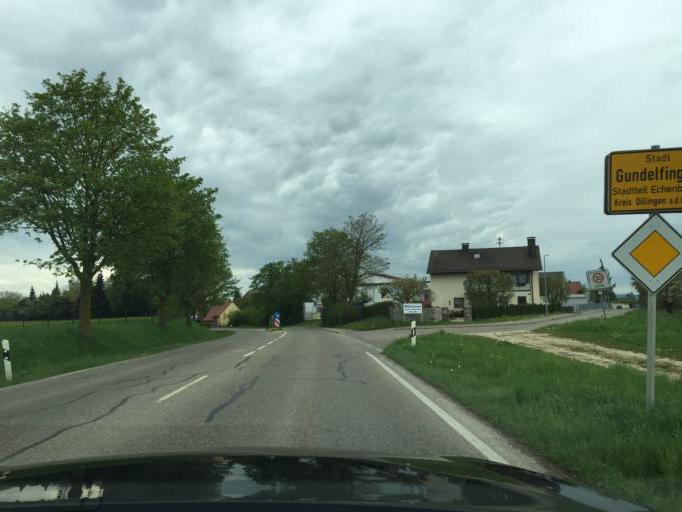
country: DE
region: Bavaria
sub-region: Swabia
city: Gundelfingen
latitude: 48.5609
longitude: 10.3910
